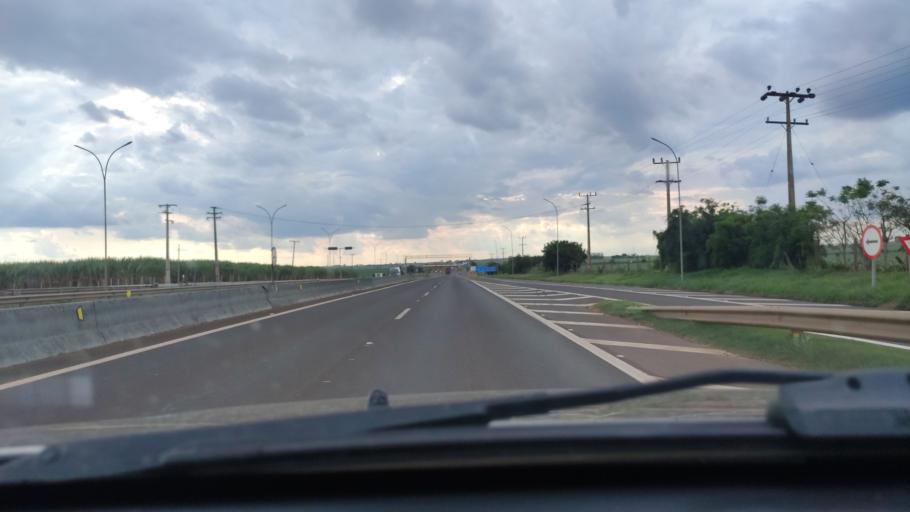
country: BR
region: Sao Paulo
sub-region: Palmital
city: Palmital
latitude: -22.7727
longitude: -50.1385
